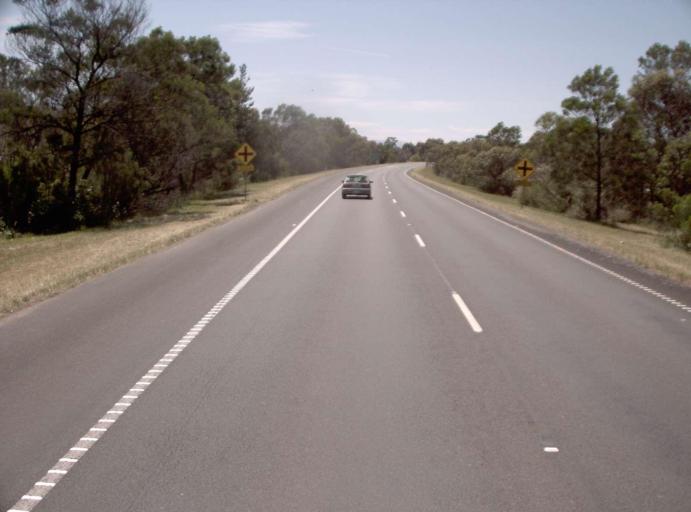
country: AU
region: Victoria
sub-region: Cardinia
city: Bunyip
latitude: -38.0769
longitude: 145.7089
